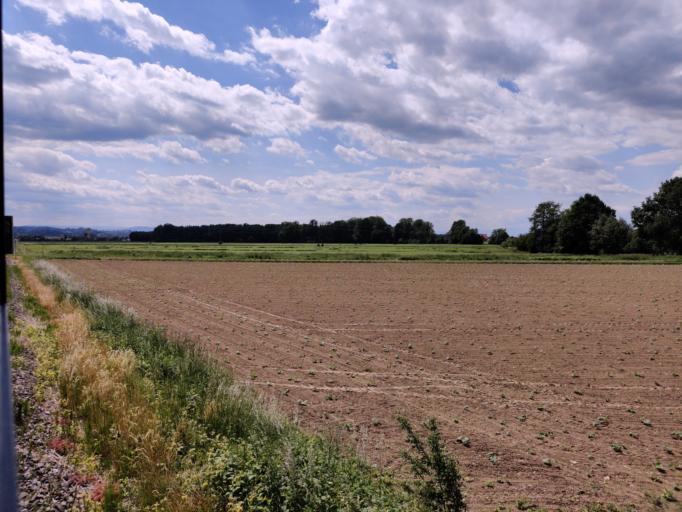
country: AT
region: Styria
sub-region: Politischer Bezirk Suedoststeiermark
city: Gosdorf
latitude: 46.7225
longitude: 15.7947
